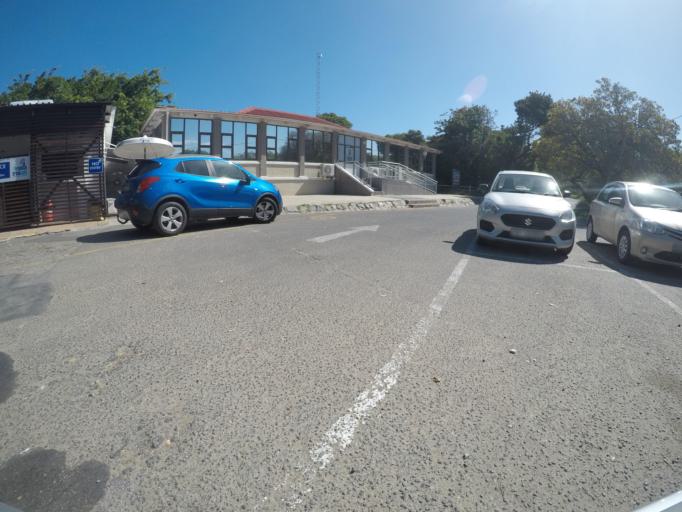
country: ZA
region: Eastern Cape
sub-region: Buffalo City Metropolitan Municipality
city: East London
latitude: -32.9857
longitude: 27.9482
